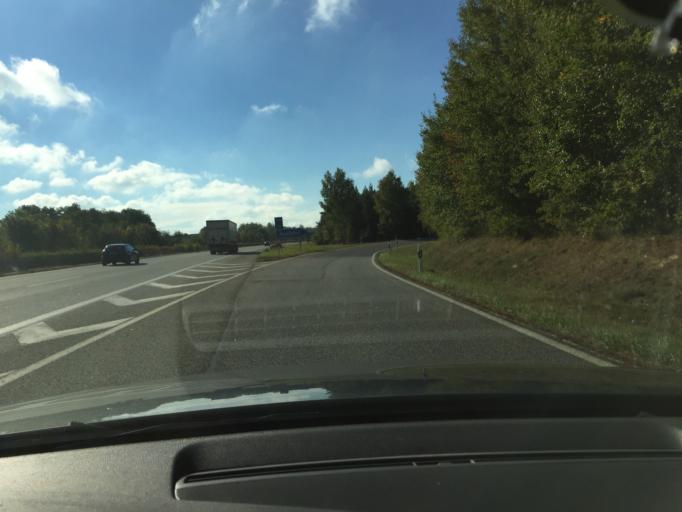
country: DE
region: Mecklenburg-Vorpommern
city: Lalendorf
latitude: 53.6866
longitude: 12.3703
